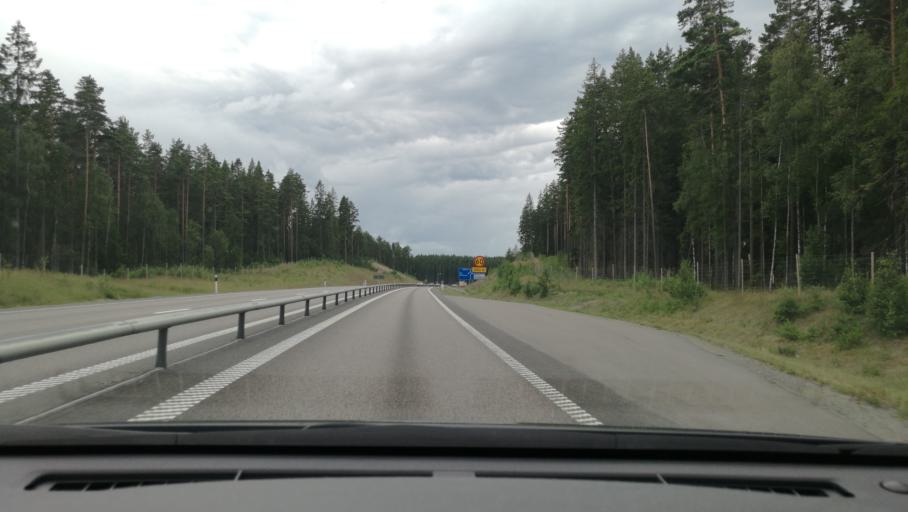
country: SE
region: Soedermanland
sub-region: Katrineholms Kommun
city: Katrineholm
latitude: 58.9759
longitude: 16.2646
